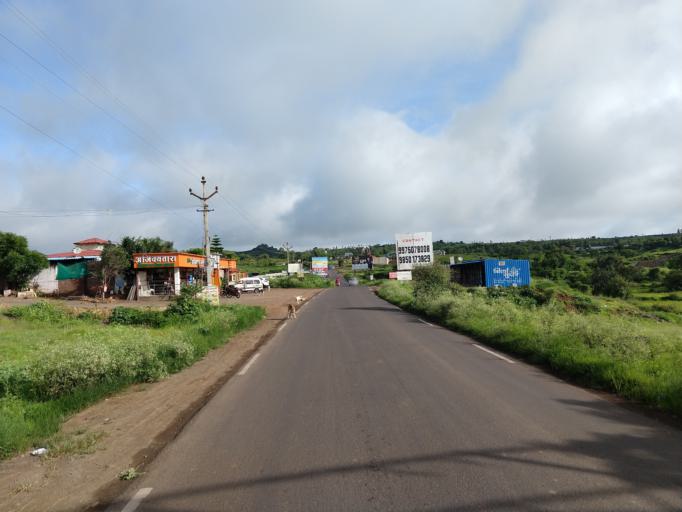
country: IN
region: Maharashtra
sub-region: Pune Division
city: Khed
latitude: 18.3966
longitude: 73.9150
